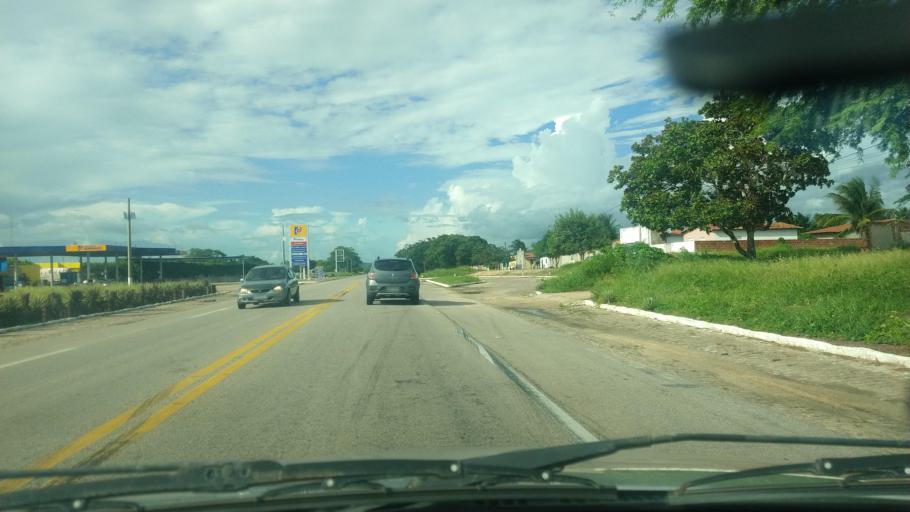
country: BR
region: Rio Grande do Norte
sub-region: Tangara
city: Tangara
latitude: -6.1743
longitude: -35.7655
